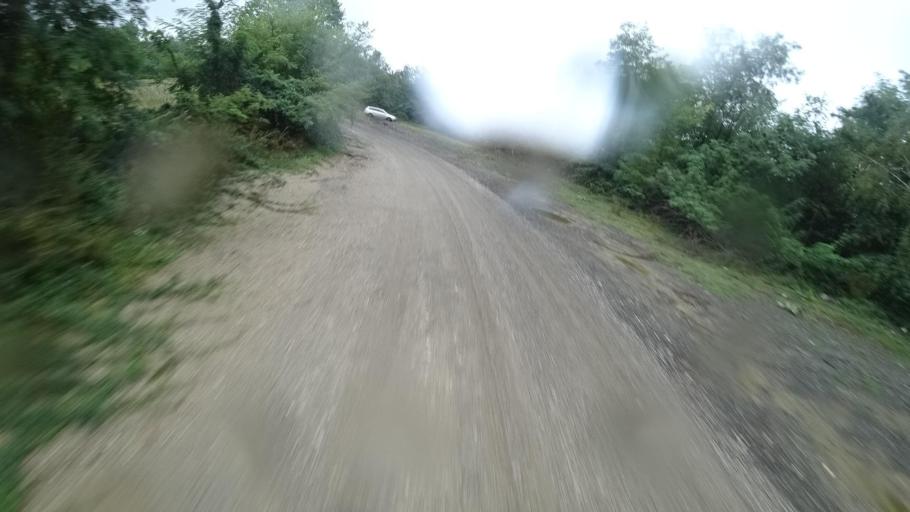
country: BA
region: Republika Srpska
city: Maricka
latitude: 44.8155
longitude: 16.8135
